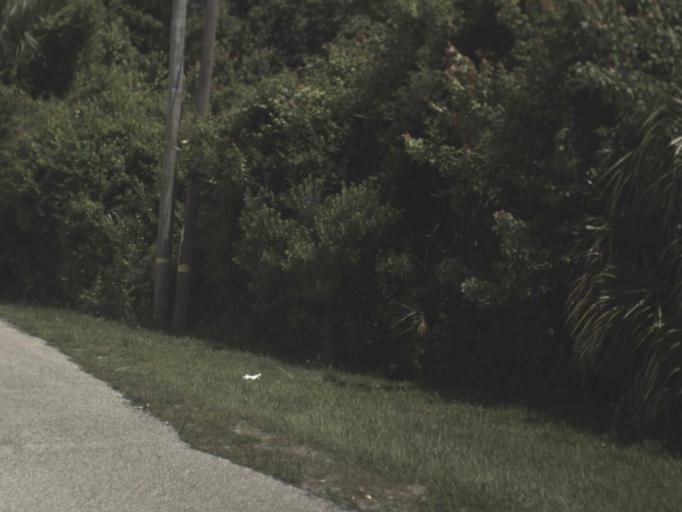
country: US
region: Florida
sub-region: Saint Johns County
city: Villano Beach
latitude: 29.9412
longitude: -81.3355
